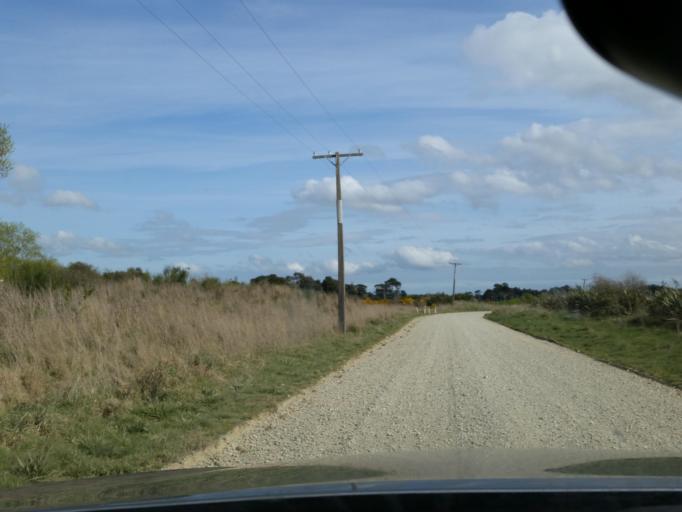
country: NZ
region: Southland
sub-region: Southland District
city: Winton
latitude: -46.2447
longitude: 168.4736
